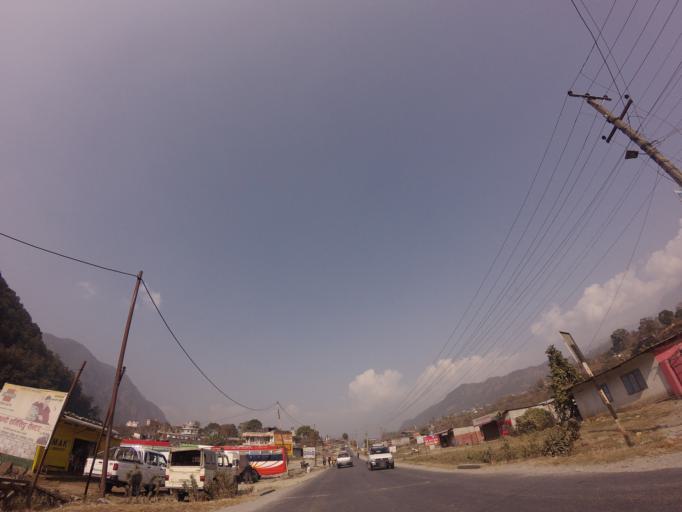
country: NP
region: Western Region
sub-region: Gandaki Zone
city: Pokhara
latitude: 28.2544
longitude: 83.9663
